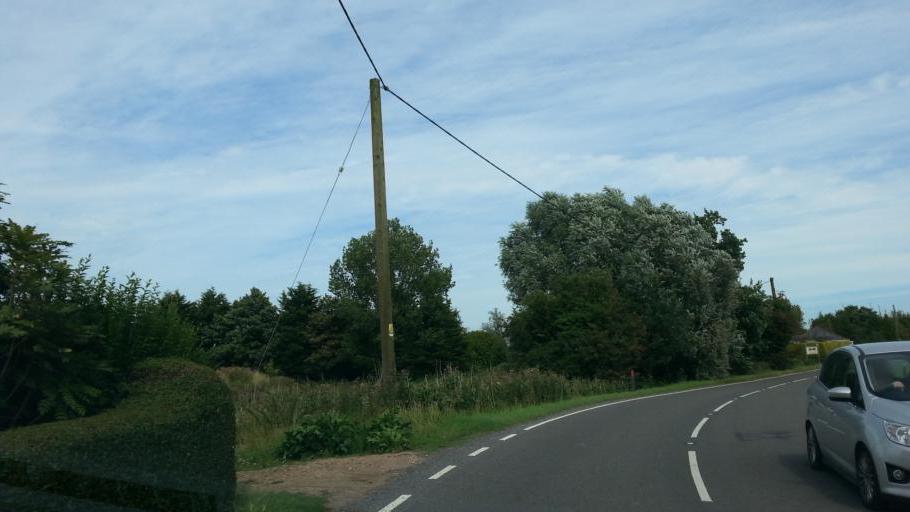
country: GB
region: England
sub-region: Norfolk
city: Outwell
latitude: 52.5845
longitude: 0.2192
